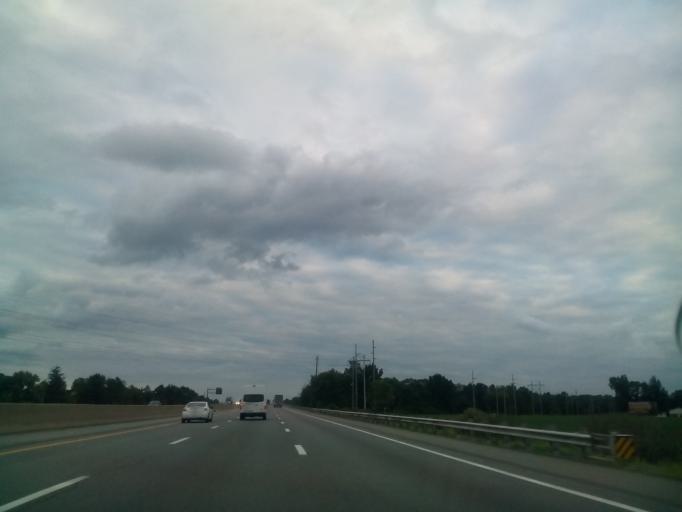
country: US
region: Ohio
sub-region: Trumbull County
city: Newton Falls
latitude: 41.1916
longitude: -80.9400
